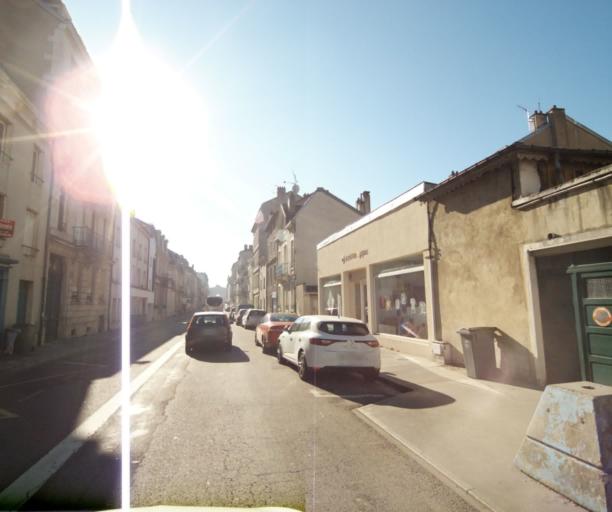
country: FR
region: Lorraine
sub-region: Departement de Meurthe-et-Moselle
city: Nancy
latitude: 48.6977
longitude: 6.1844
